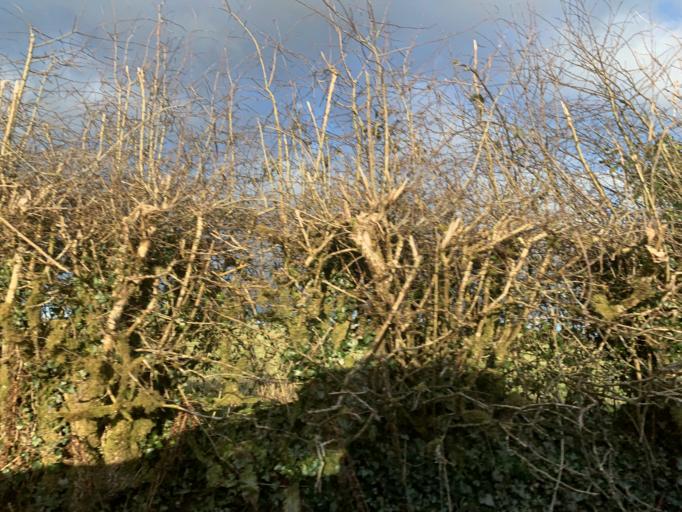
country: IE
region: Connaught
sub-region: Maigh Eo
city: Ballyhaunis
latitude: 53.8137
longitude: -8.6943
